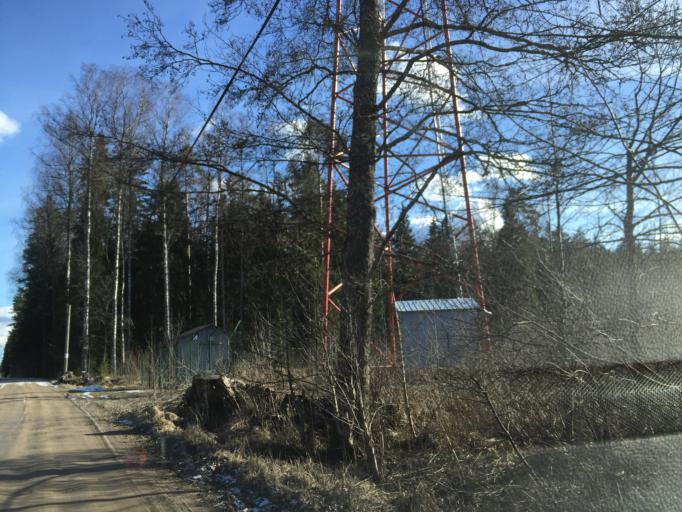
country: LV
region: Garkalne
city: Garkalne
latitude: 56.9534
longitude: 24.4414
